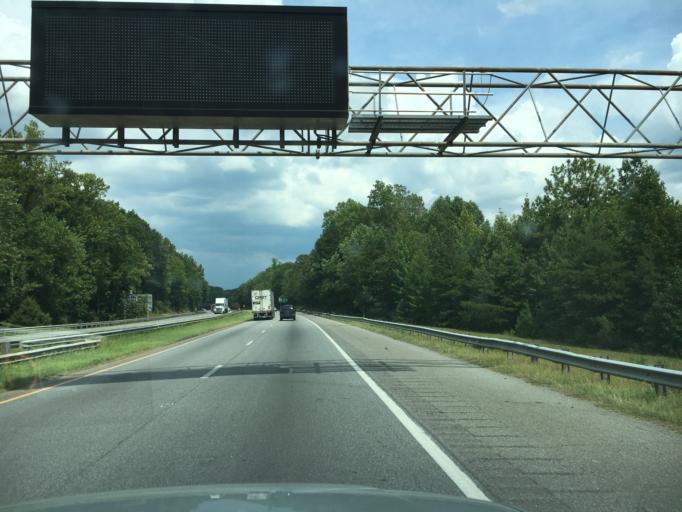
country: US
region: North Carolina
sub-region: Cleveland County
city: Kings Mountain
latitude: 35.2335
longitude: -81.3191
